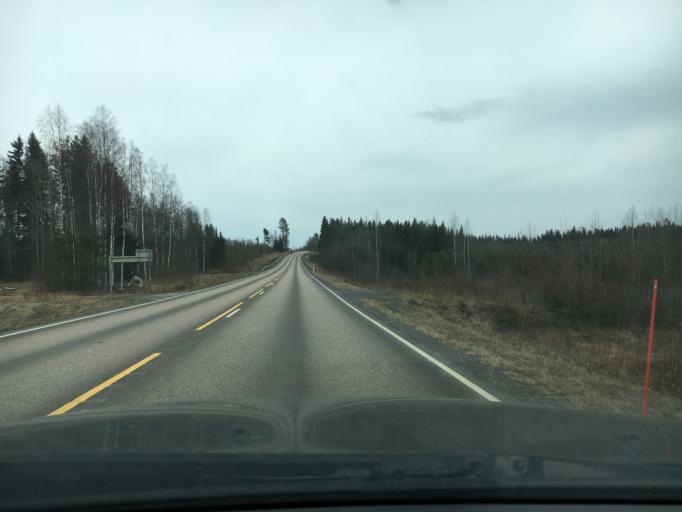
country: FI
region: Central Finland
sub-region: AEaenekoski
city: Konnevesi
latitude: 62.6940
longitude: 26.4244
